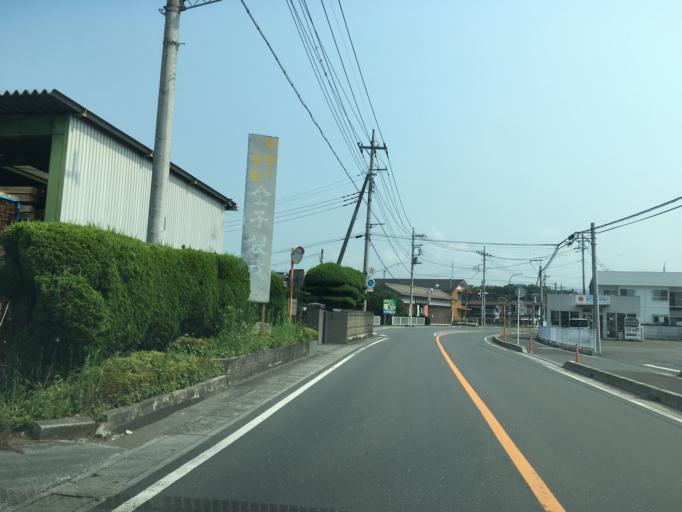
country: JP
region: Saitama
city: Chichibu
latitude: 36.0054
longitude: 139.1084
